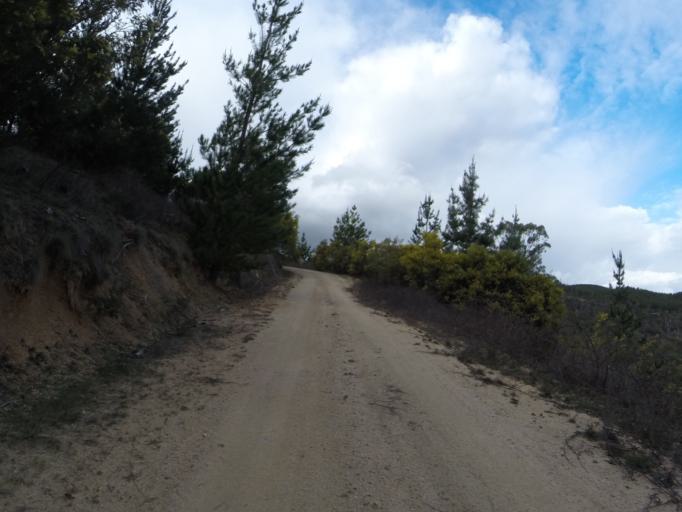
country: AU
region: Australian Capital Territory
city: Macquarie
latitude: -35.3498
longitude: 148.9496
